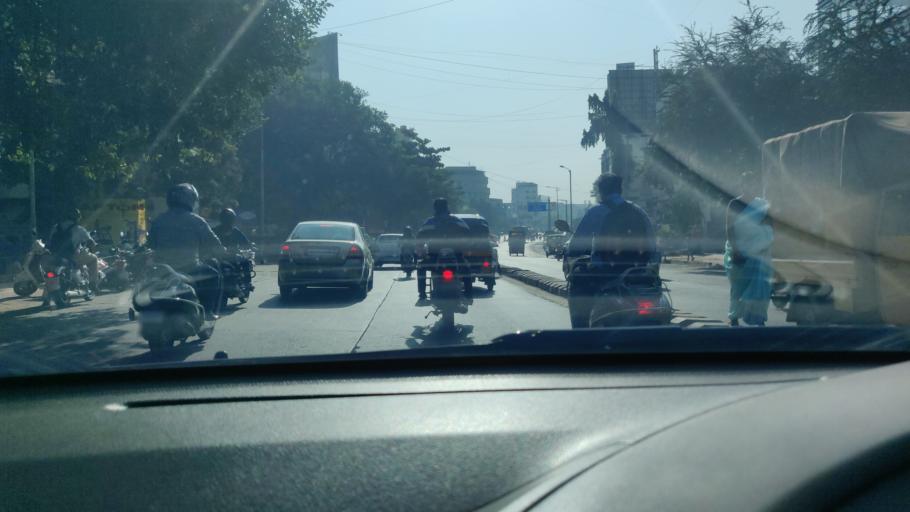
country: IN
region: Maharashtra
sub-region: Pune Division
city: Khadki
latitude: 18.5580
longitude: 73.7929
